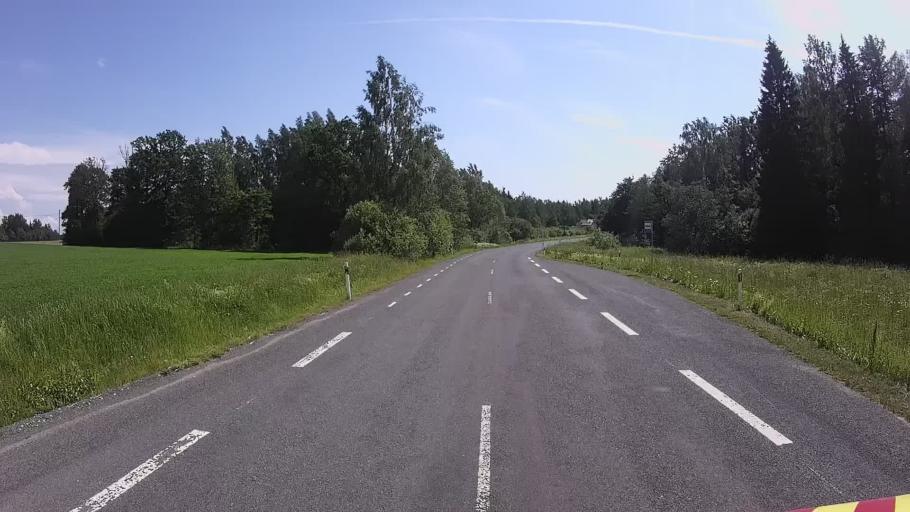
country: EE
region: Viljandimaa
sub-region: Karksi vald
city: Karksi-Nuia
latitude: 58.0889
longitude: 25.5583
